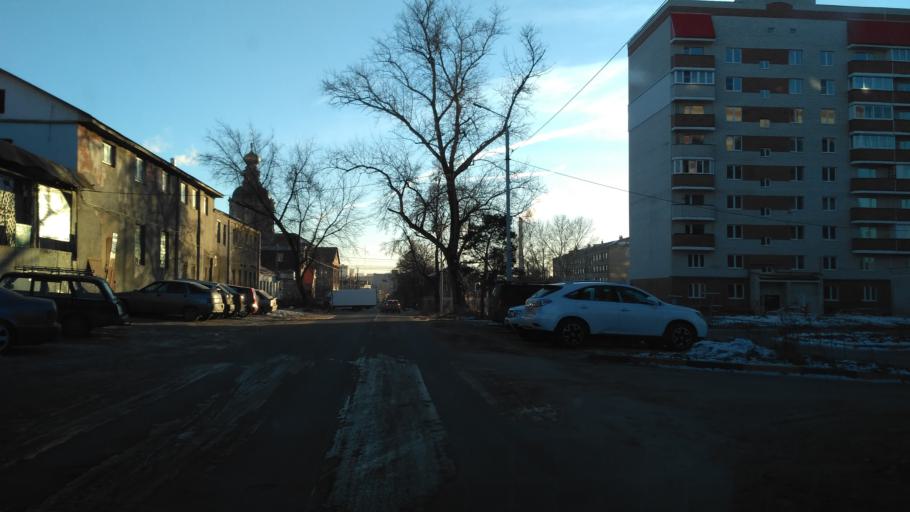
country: RU
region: Tula
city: Tula
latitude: 54.2083
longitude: 37.6115
